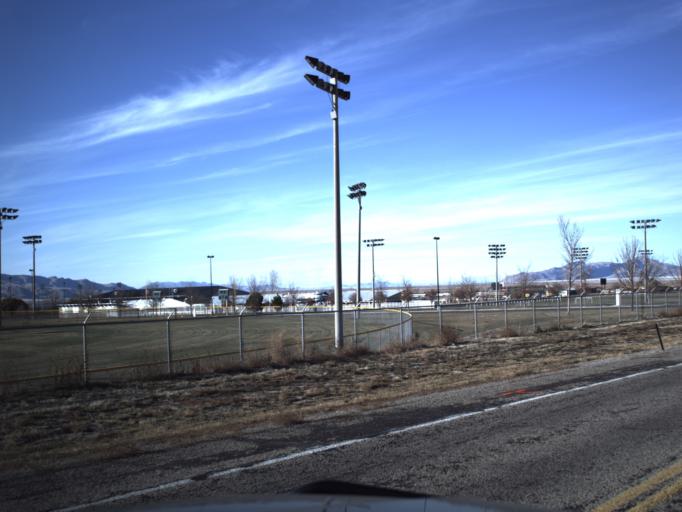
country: US
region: Utah
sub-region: Tooele County
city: Erda
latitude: 40.5689
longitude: -112.3672
